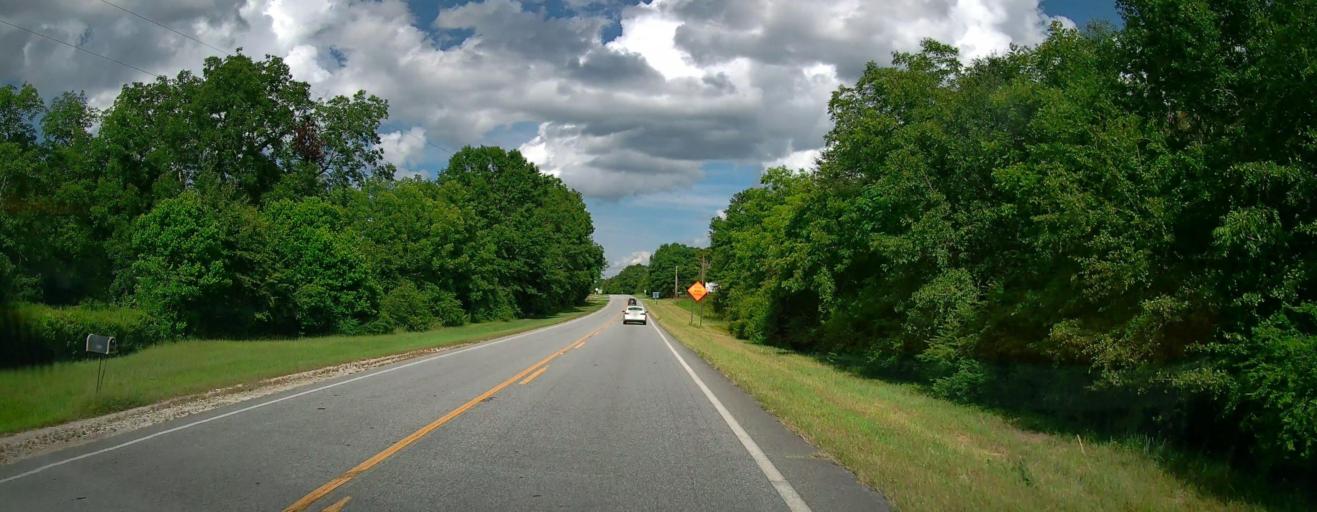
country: US
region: Alabama
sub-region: Lee County
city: Opelika
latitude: 32.4398
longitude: -85.3089
